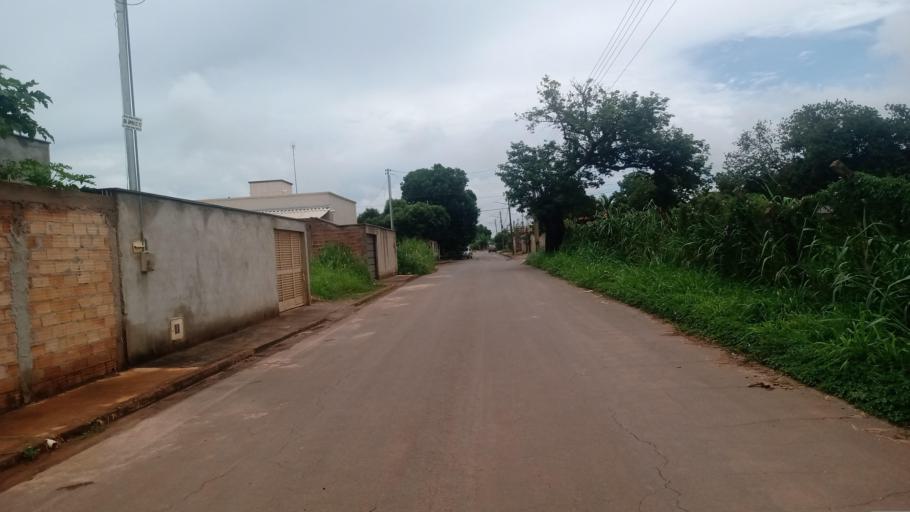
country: BR
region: Goias
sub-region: Senador Canedo
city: Senador Canedo
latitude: -16.7200
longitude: -49.1164
